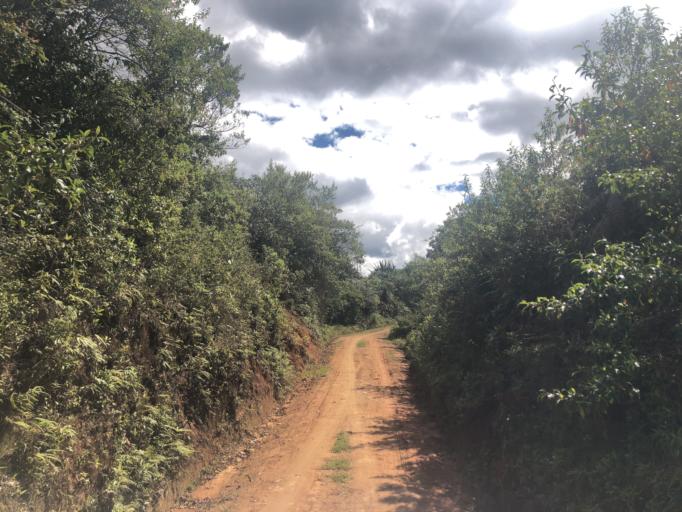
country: CO
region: Cauca
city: Silvia
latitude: 2.6783
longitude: -76.4405
